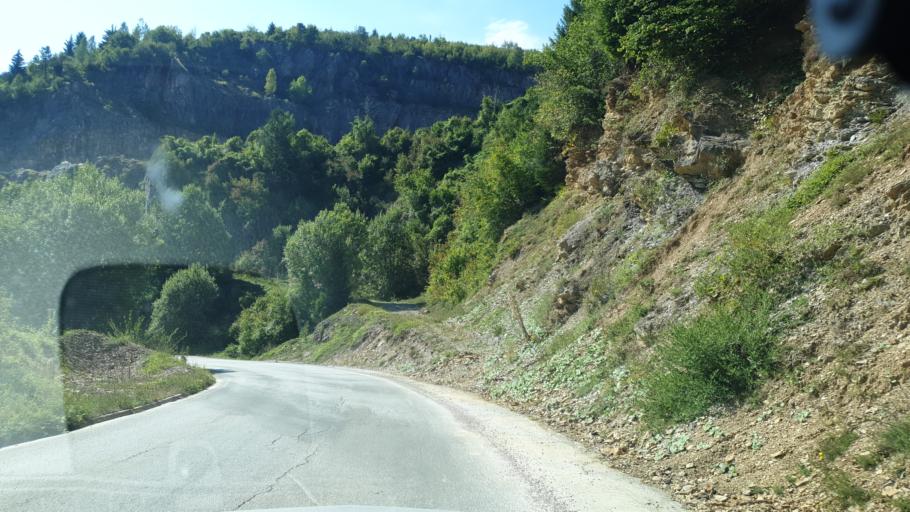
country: RS
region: Central Serbia
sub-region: Zlatiborski Okrug
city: Nova Varos
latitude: 43.4199
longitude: 19.9238
